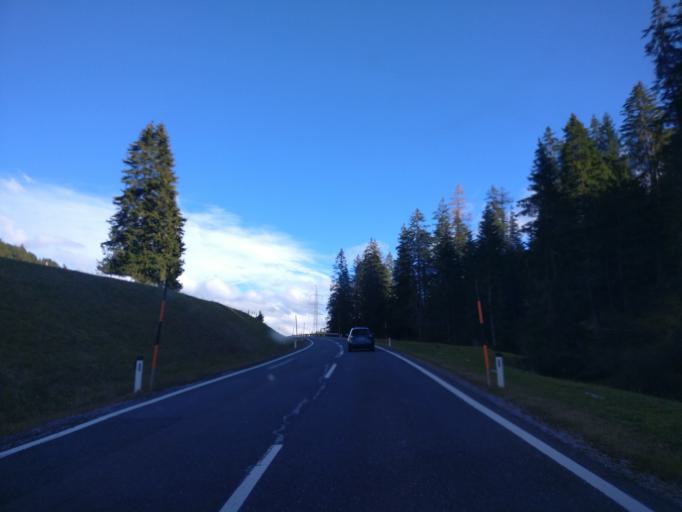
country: AT
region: Salzburg
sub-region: Politischer Bezirk Zell am See
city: Dienten am Hochkonig
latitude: 47.3917
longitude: 13.0441
